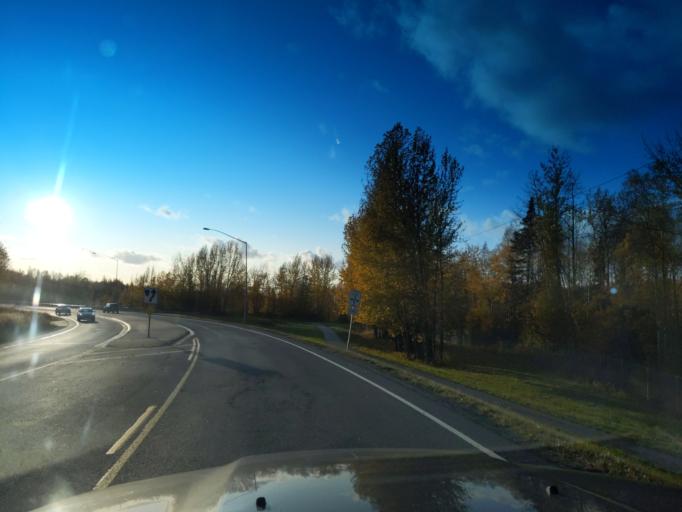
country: US
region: Alaska
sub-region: Anchorage Municipality
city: Anchorage
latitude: 61.1665
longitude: -149.9487
